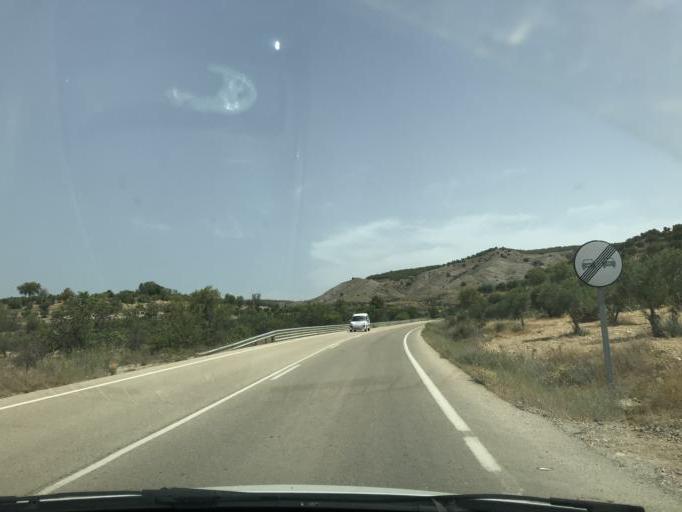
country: ES
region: Castille-La Mancha
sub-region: Provincia de Cuenca
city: Albalate de las Nogueras
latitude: 40.3754
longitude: -2.2760
